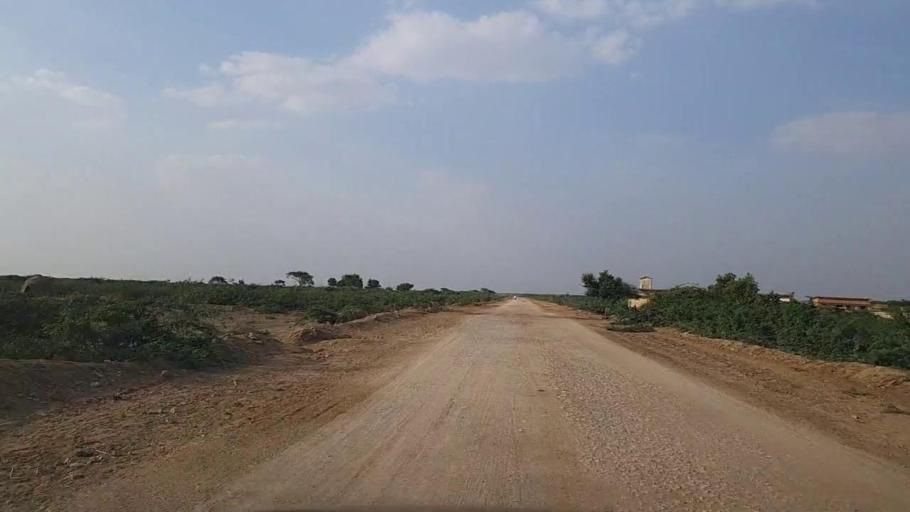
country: PK
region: Sindh
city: Gharo
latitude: 24.7997
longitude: 67.7440
